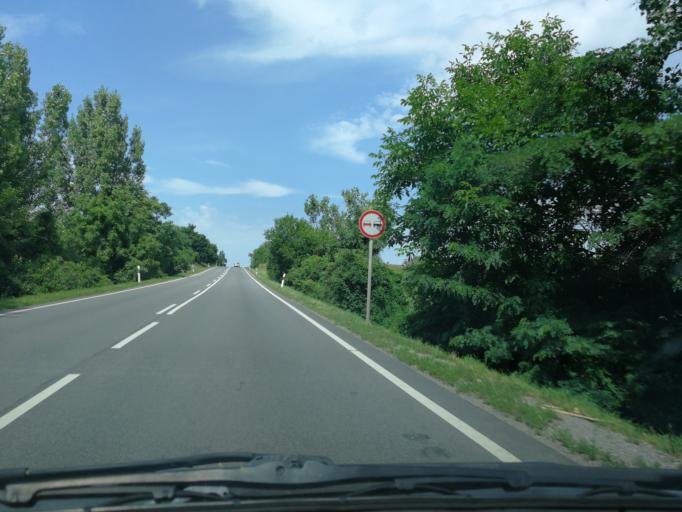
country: HU
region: Baranya
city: Pecsvarad
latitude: 46.1430
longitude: 18.4091
